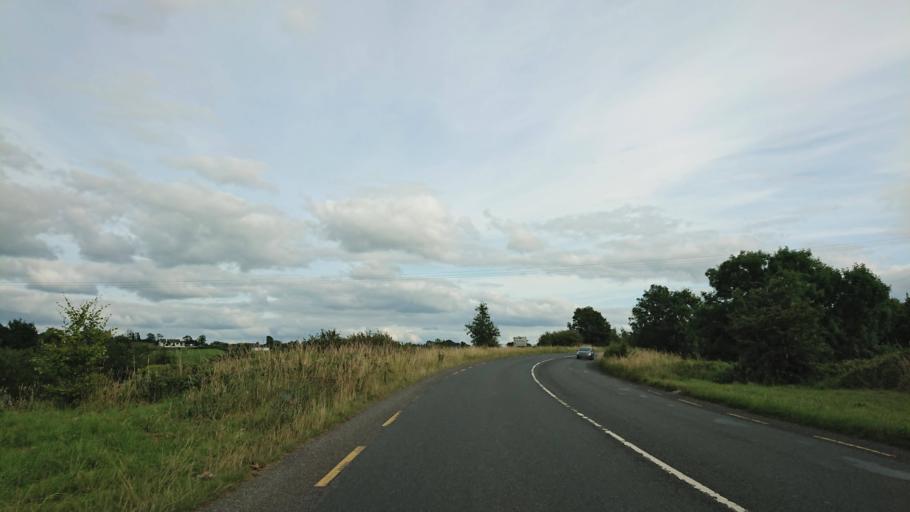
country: IE
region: Connaught
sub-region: County Leitrim
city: Carrick-on-Shannon
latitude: 53.9788
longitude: -8.0622
